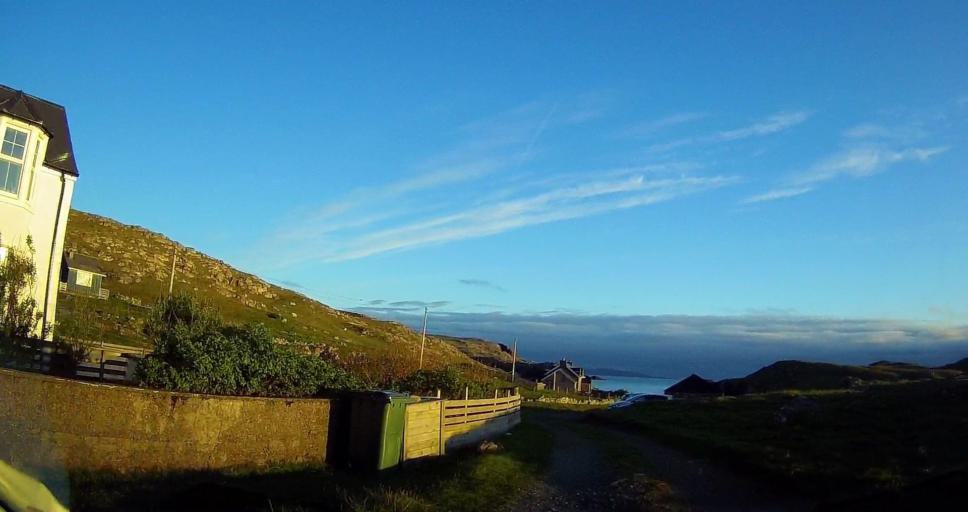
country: GB
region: Scotland
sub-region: Shetland Islands
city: Lerwick
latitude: 60.4413
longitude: -1.4476
